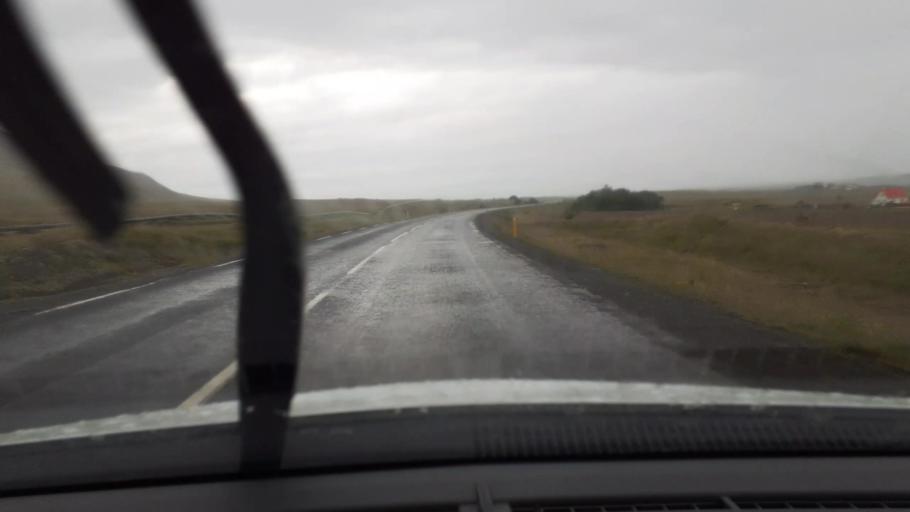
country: IS
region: West
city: Borgarnes
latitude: 64.3656
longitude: -21.8996
